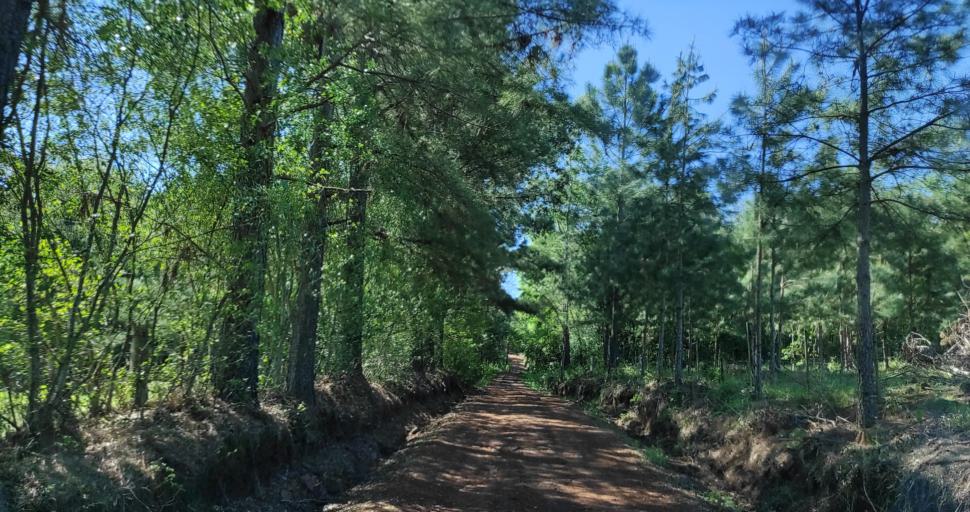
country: AR
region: Misiones
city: Ruiz de Montoya
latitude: -26.9464
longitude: -55.0028
